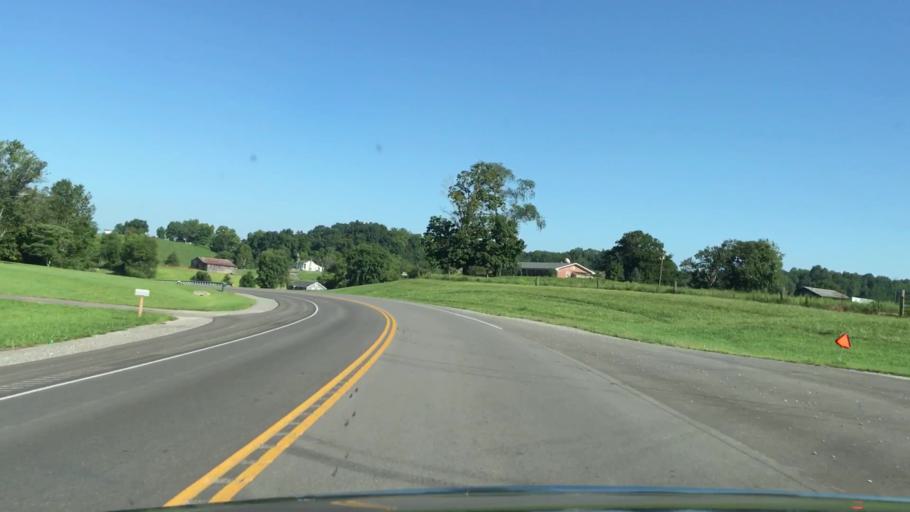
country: US
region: Kentucky
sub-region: Cumberland County
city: Burkesville
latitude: 36.7536
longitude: -85.3700
